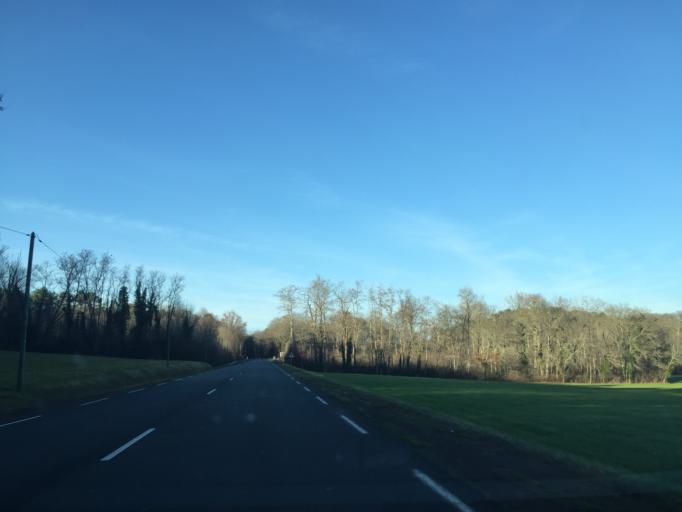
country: FR
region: Aquitaine
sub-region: Departement de la Dordogne
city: Riberac
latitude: 45.1779
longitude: 0.3864
